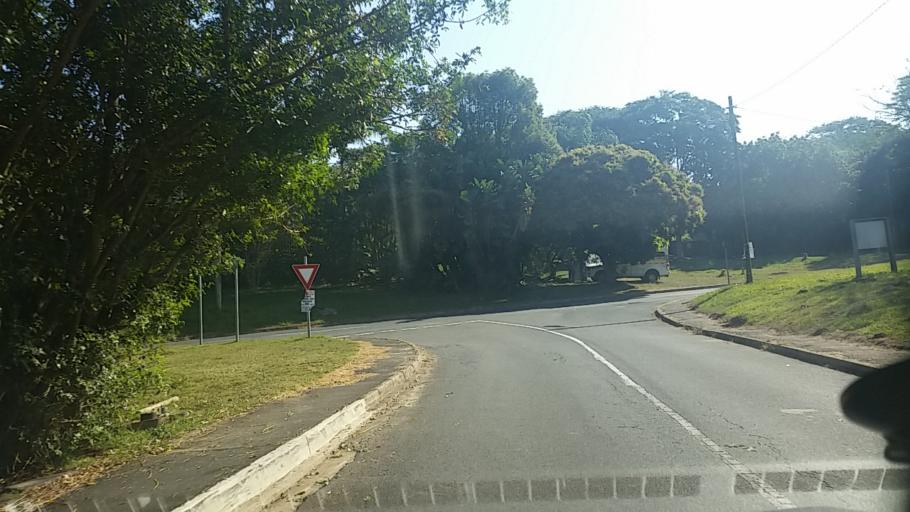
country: ZA
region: KwaZulu-Natal
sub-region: eThekwini Metropolitan Municipality
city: Berea
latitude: -29.8430
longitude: 30.9056
